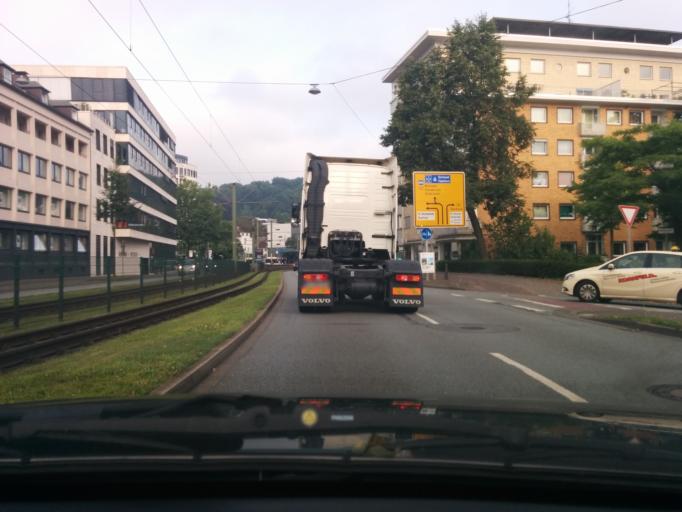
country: DE
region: North Rhine-Westphalia
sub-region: Regierungsbezirk Detmold
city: Bielefeld
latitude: 52.0171
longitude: 8.5274
